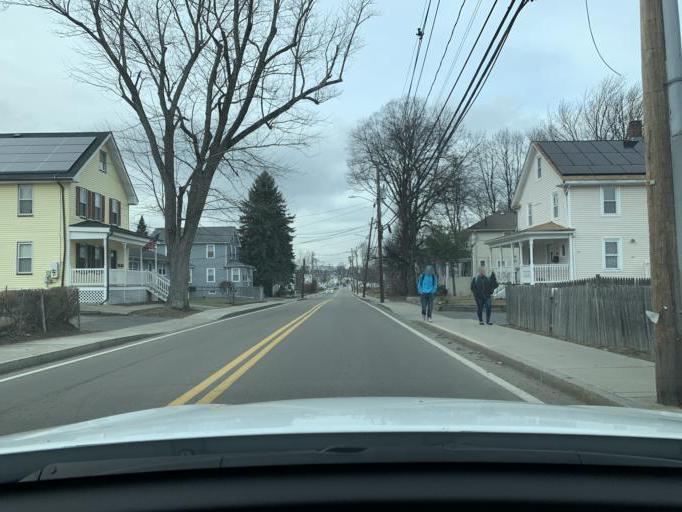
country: US
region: Massachusetts
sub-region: Middlesex County
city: Framingham
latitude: 42.2746
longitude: -71.4032
